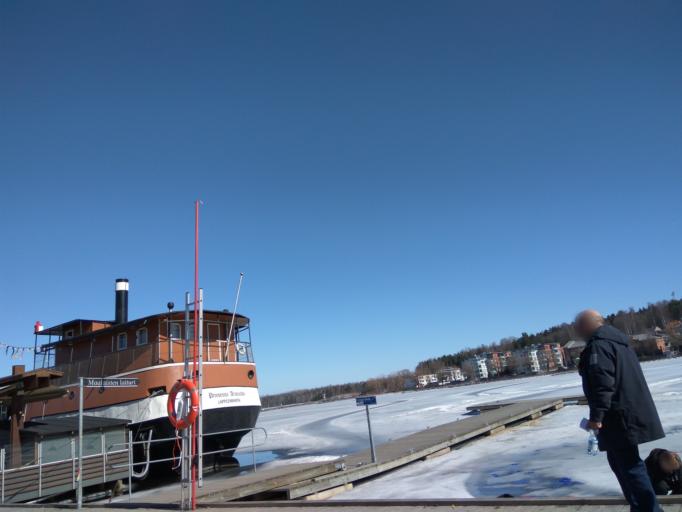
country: FI
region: South Karelia
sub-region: Lappeenranta
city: Lappeenranta
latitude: 61.0618
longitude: 28.1870
